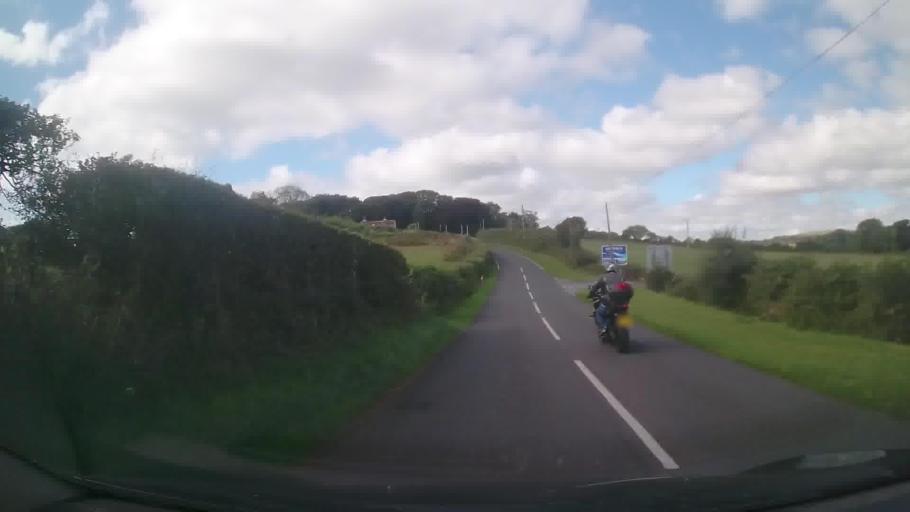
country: GB
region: Wales
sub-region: Pembrokeshire
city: Penally
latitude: 51.6564
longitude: -4.7541
